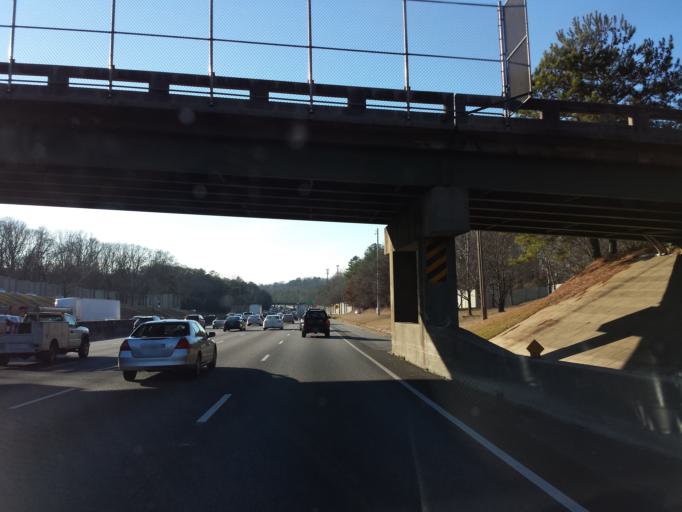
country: US
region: Georgia
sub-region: Fulton County
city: Sandy Springs
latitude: 33.9161
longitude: -84.4066
